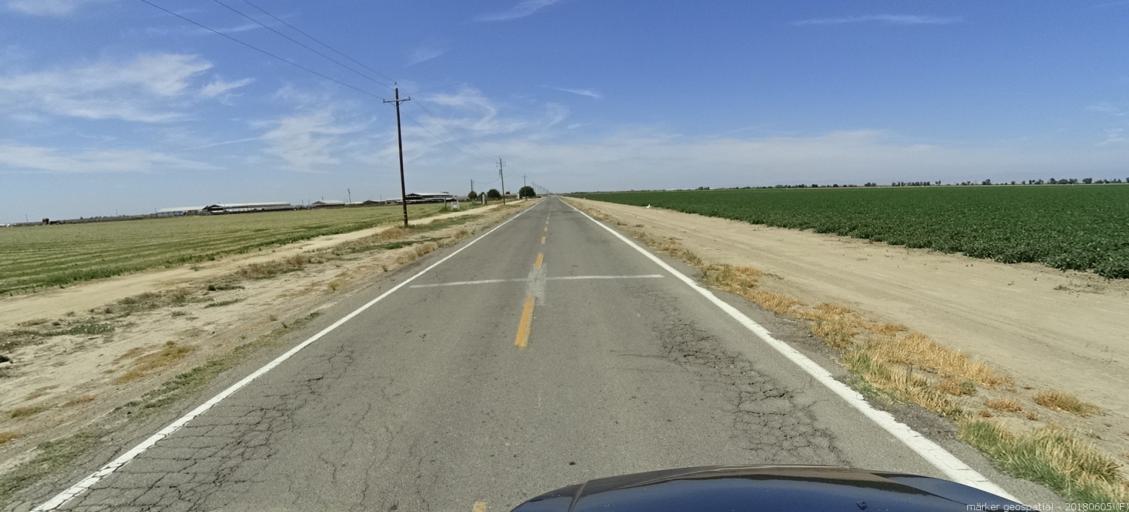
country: US
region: California
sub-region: Fresno County
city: Firebaugh
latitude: 36.9843
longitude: -120.3830
